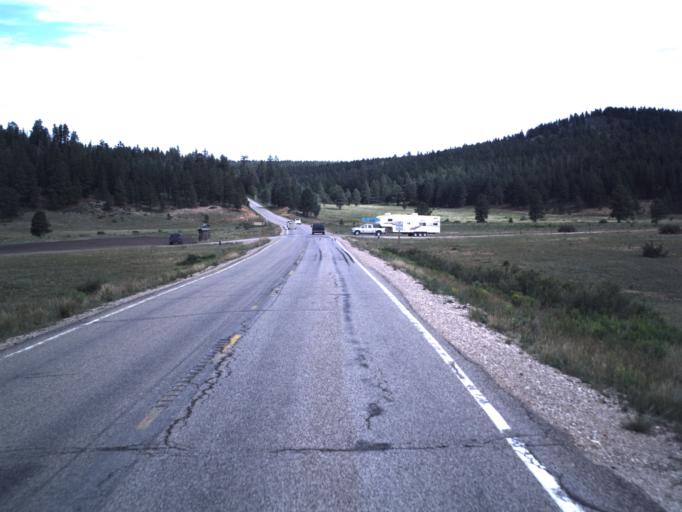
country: US
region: Utah
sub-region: Garfield County
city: Panguitch
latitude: 37.5028
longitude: -112.6239
